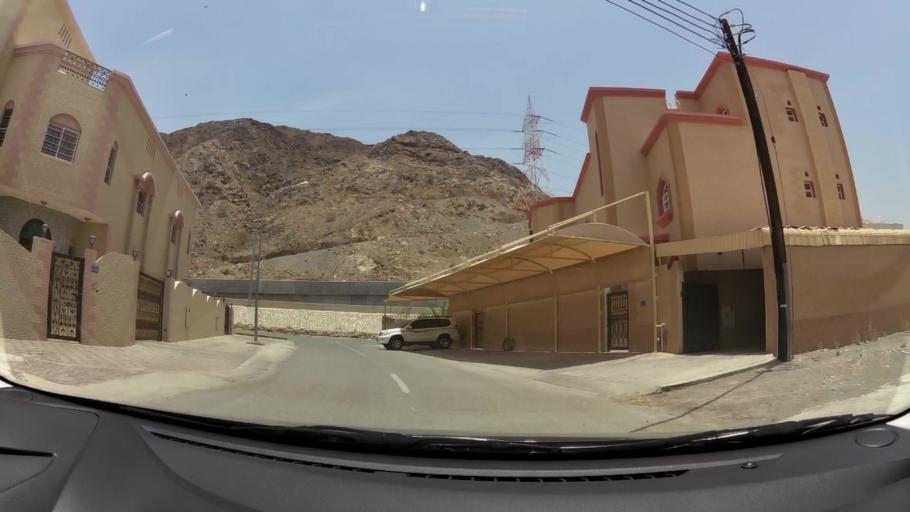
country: OM
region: Muhafazat Masqat
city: Bawshar
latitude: 23.5689
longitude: 58.4289
